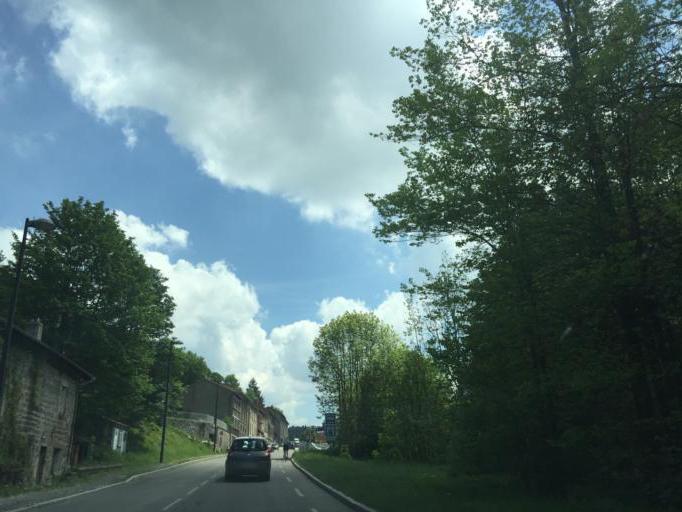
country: FR
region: Rhone-Alpes
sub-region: Departement de la Loire
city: Saint-Genest-Malifaux
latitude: 45.3786
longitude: 4.4409
